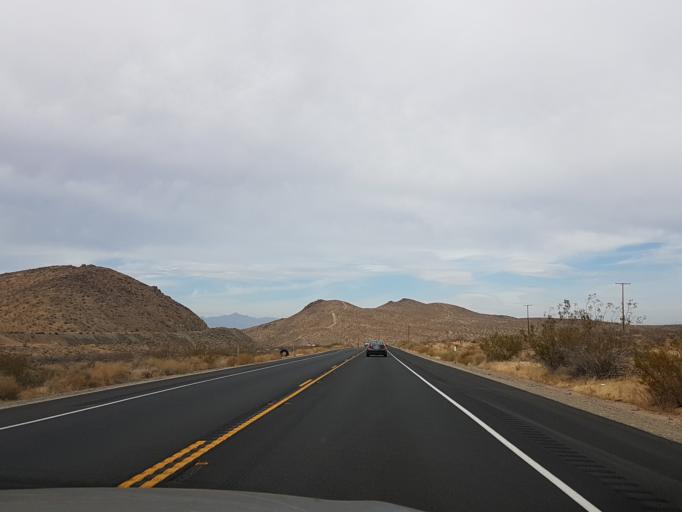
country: US
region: California
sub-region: Kern County
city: Ridgecrest
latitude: 35.5395
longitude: -117.6863
